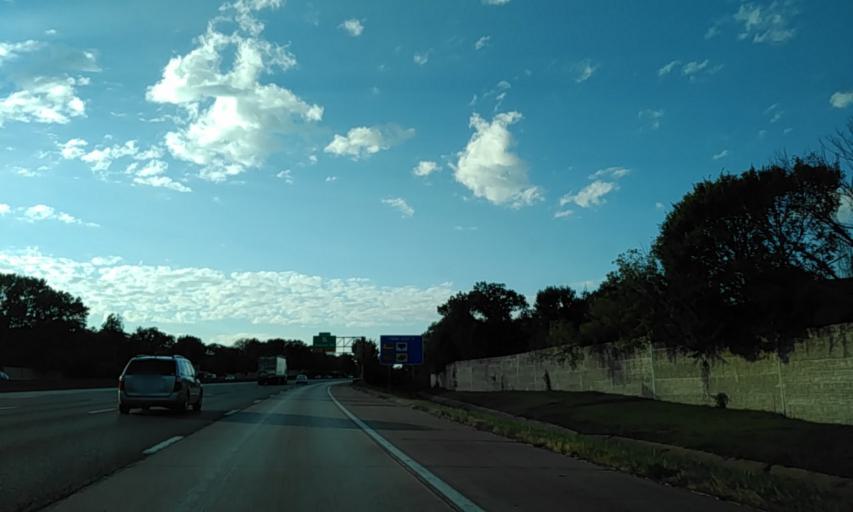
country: US
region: Missouri
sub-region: Saint Louis County
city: Sappington
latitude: 38.5182
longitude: -90.3885
